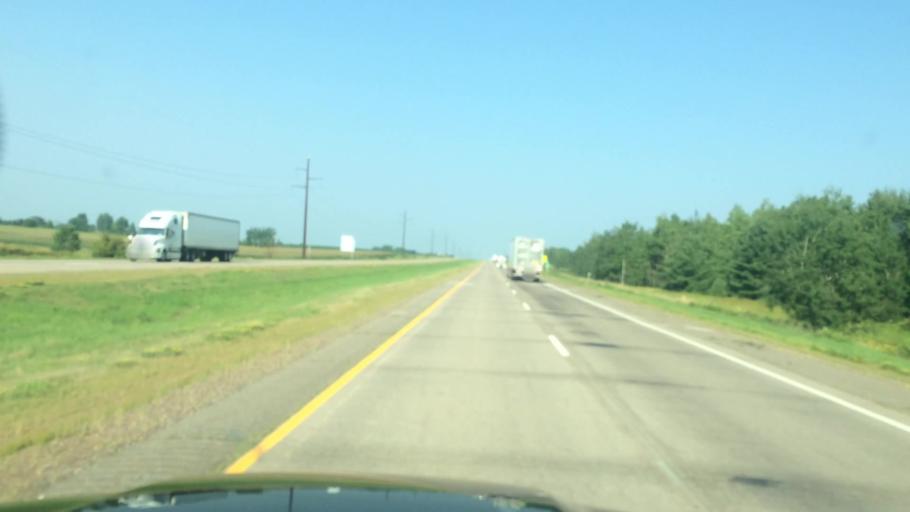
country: US
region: Wisconsin
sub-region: Marathon County
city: Edgar
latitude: 44.9445
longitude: -89.9767
